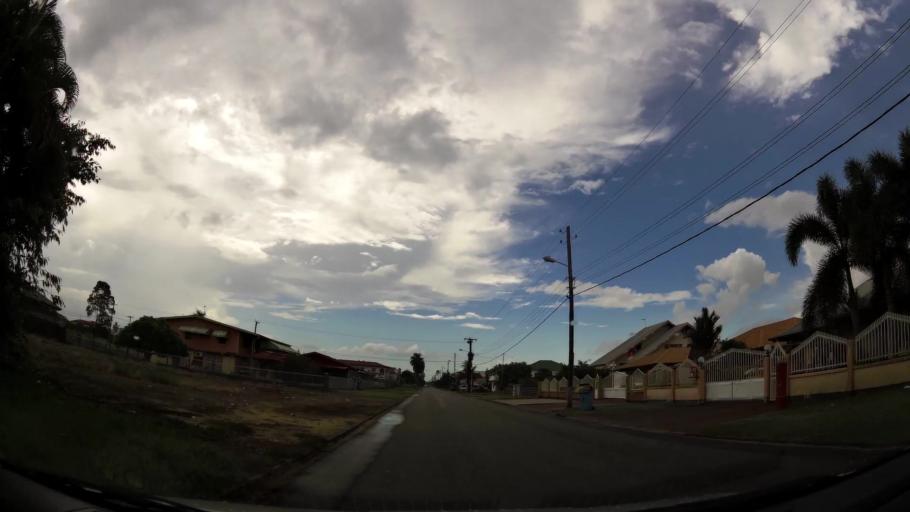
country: SR
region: Paramaribo
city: Paramaribo
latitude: 5.8418
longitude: -55.1227
